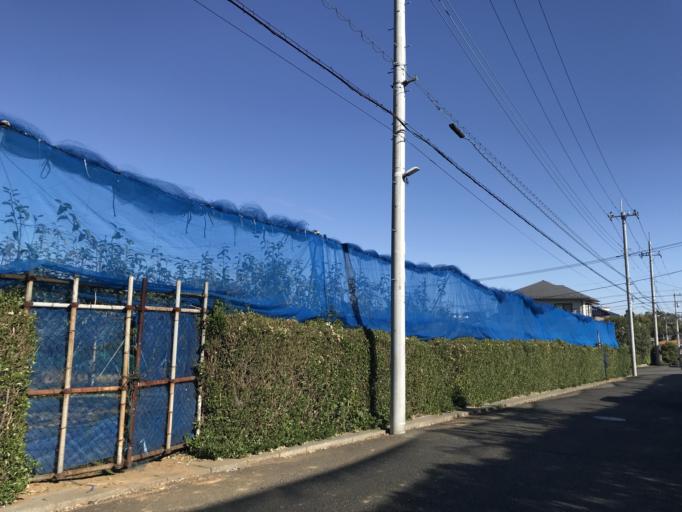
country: JP
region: Tokyo
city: Chofugaoka
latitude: 35.5741
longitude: 139.5809
